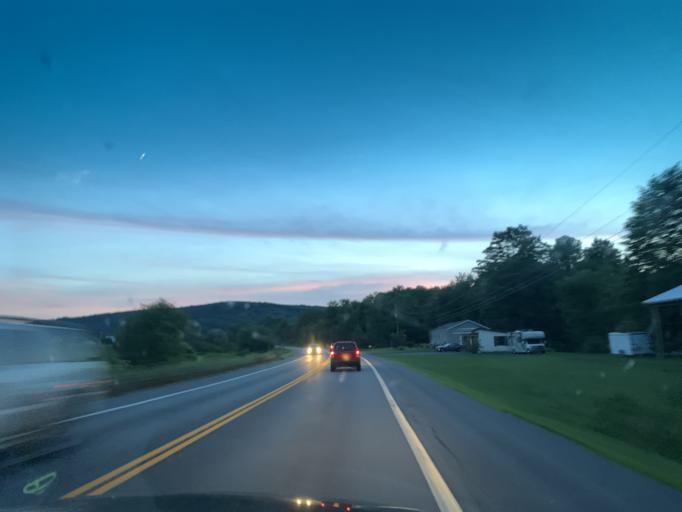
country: US
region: New York
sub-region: Chenango County
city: New Berlin
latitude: 42.5652
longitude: -75.3493
